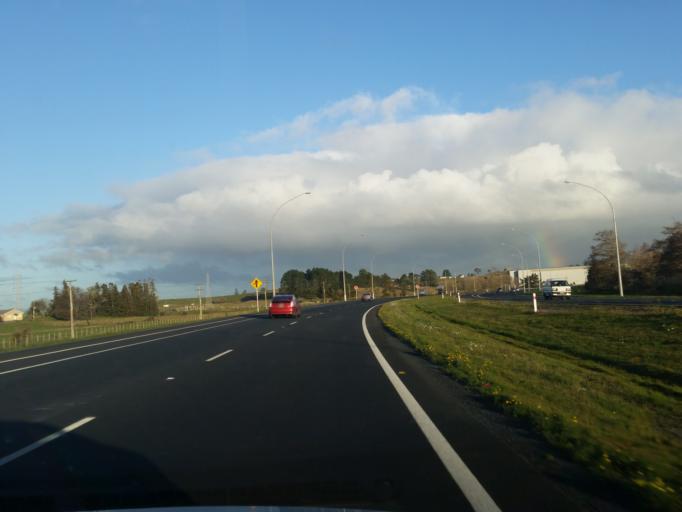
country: NZ
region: Waikato
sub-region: Waikato District
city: Te Kauwhata
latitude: -37.3065
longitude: 175.0664
